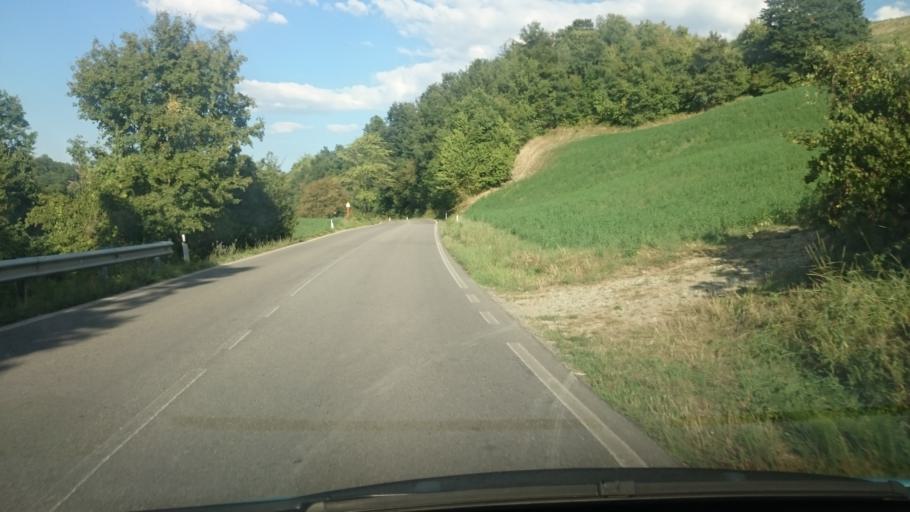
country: IT
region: Emilia-Romagna
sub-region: Provincia di Reggio Emilia
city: Carpineti
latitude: 44.4049
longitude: 10.5092
